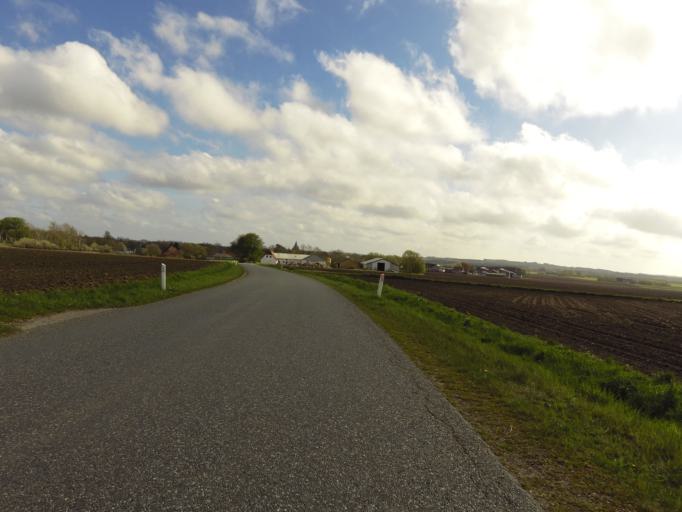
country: DK
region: South Denmark
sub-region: Haderslev Kommune
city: Gram
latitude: 55.3214
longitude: 8.9813
